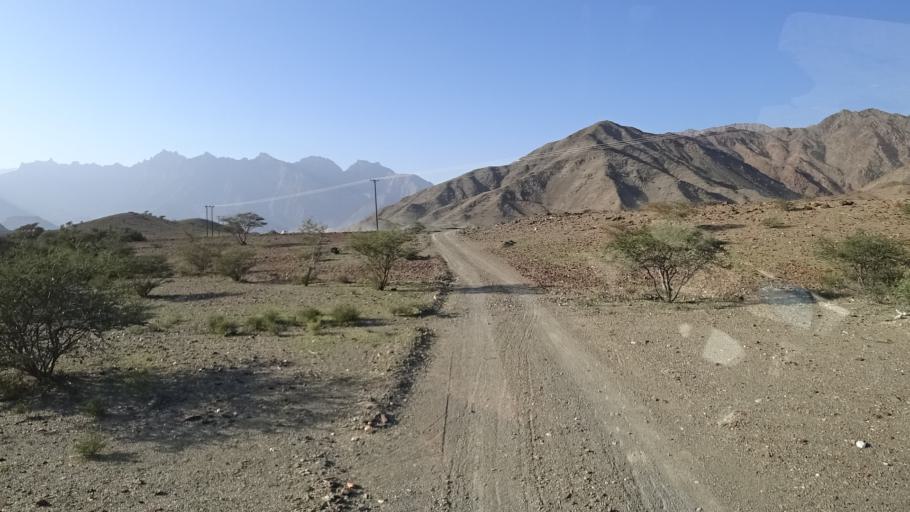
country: OM
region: Al Batinah
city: Rustaq
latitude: 23.2751
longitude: 57.3606
